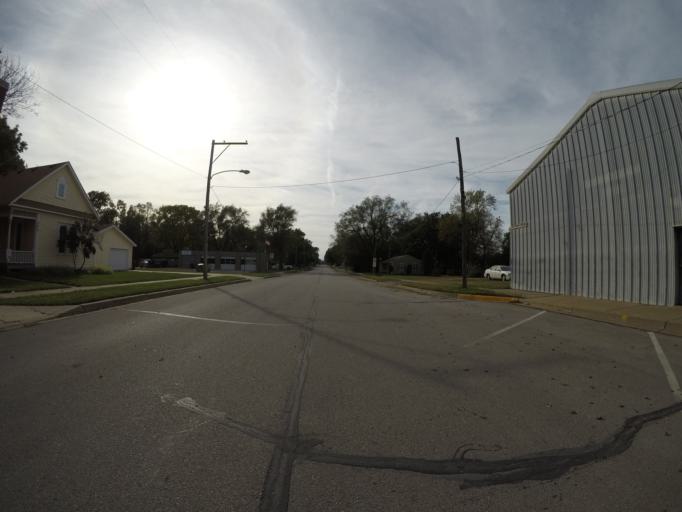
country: US
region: Kansas
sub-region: Johnson County
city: Edgerton
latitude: 38.7649
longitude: -95.0076
